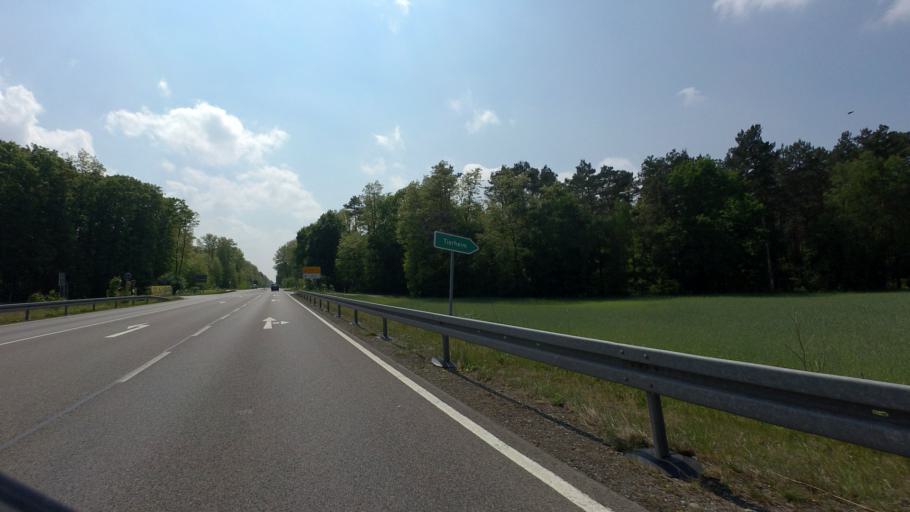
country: DE
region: Brandenburg
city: Spremberg
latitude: 51.6522
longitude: 14.3612
